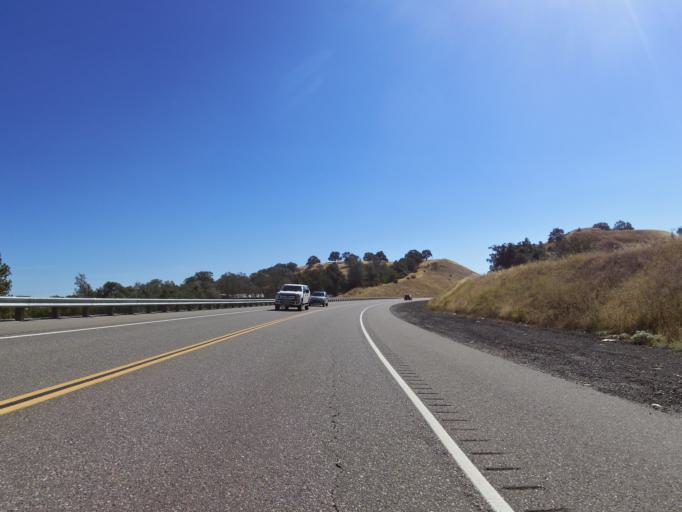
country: US
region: California
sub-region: Calaveras County
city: Angels Camp
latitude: 38.0853
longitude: -120.5527
